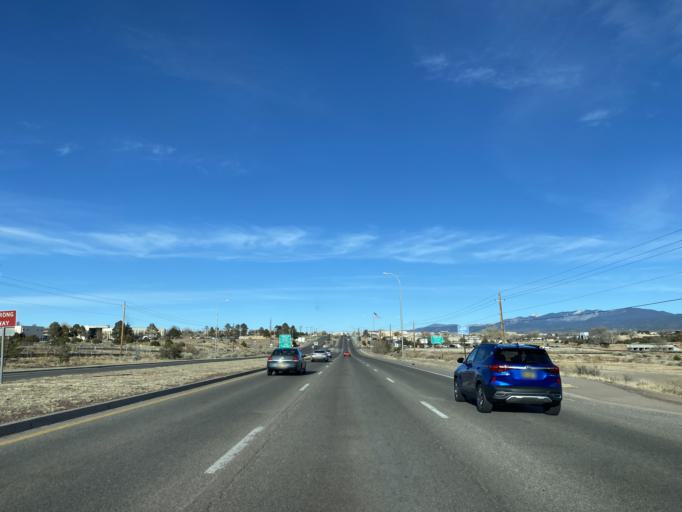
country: US
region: New Mexico
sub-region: Santa Fe County
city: Agua Fria
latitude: 35.6251
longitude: -106.0258
